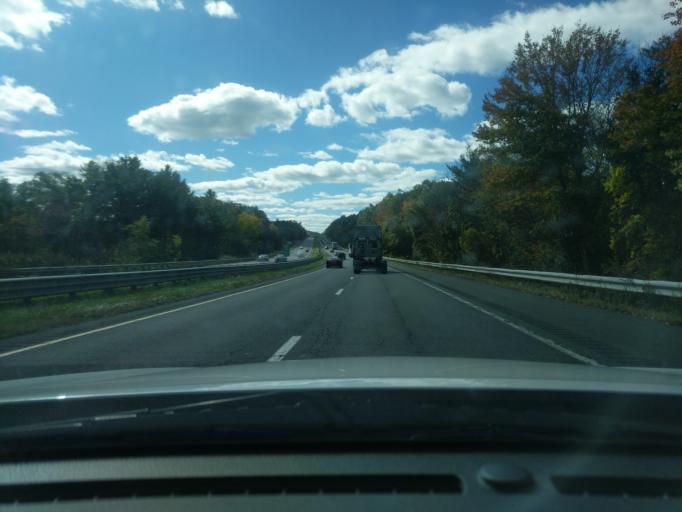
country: US
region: Massachusetts
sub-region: Hampden County
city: Chicopee
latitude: 42.1490
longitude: -72.6706
